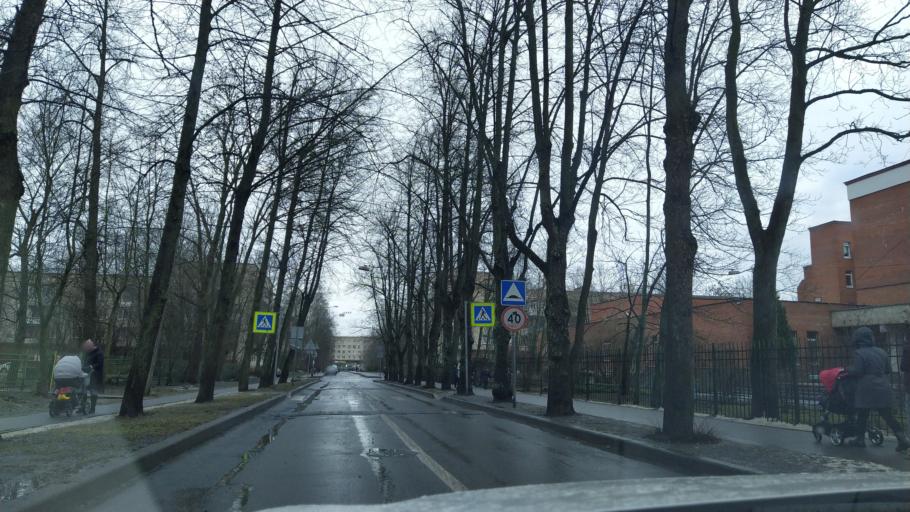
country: RU
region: St.-Petersburg
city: Pushkin
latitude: 59.7252
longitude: 30.4106
